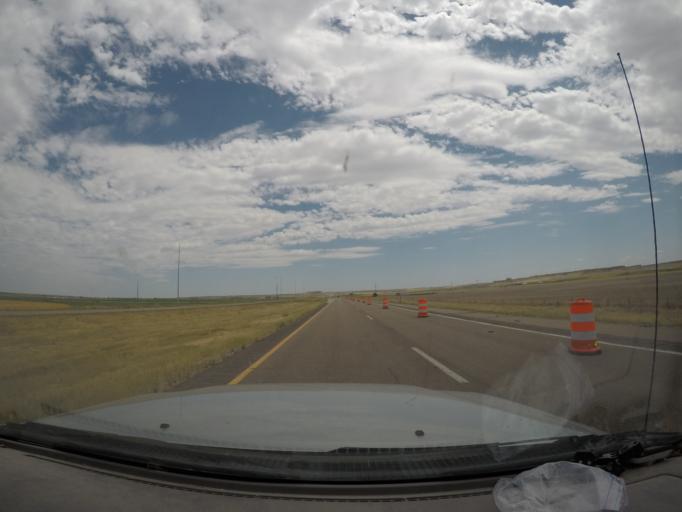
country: US
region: Nebraska
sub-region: Cheyenne County
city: Sidney
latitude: 41.1380
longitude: -103.0562
